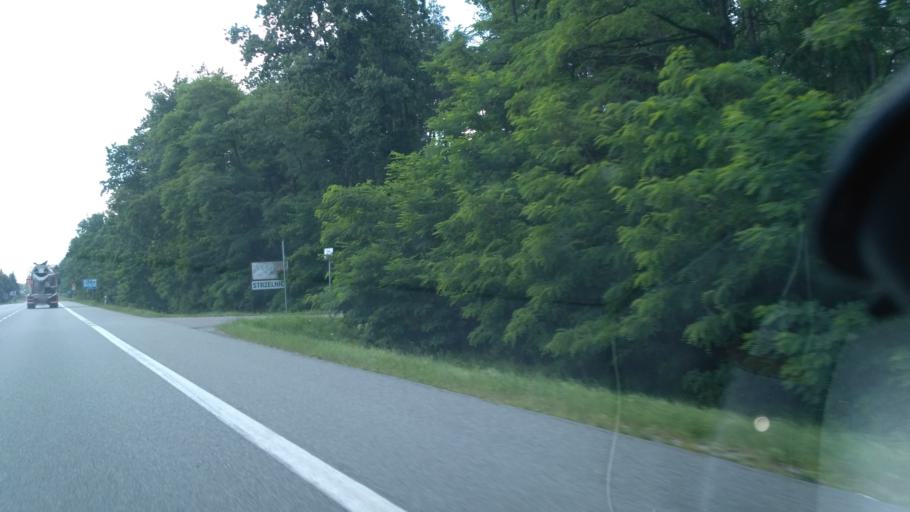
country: PL
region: Subcarpathian Voivodeship
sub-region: Powiat rzeszowski
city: Rudna Mala
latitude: 50.1239
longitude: 21.9696
